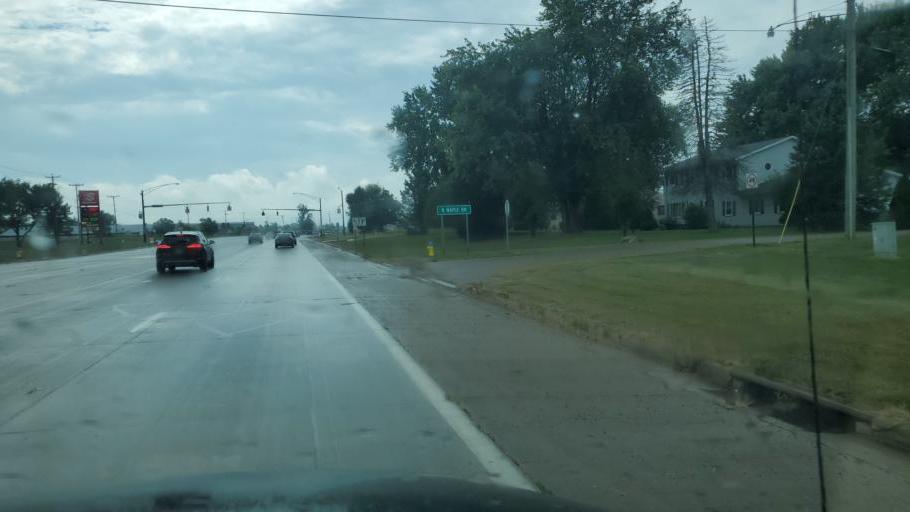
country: US
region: Ohio
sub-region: Licking County
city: Hebron
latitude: 39.9813
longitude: -82.4860
